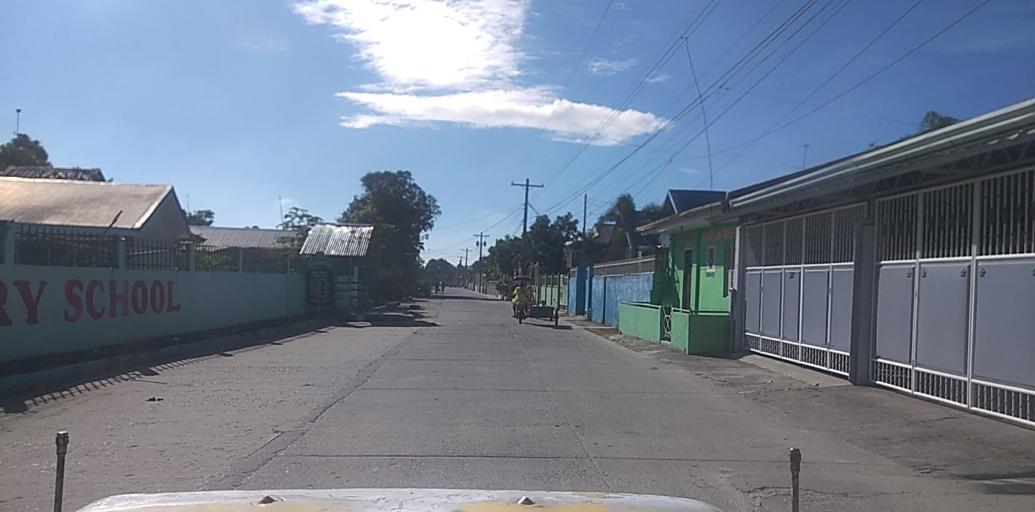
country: PH
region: Central Luzon
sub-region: Province of Pampanga
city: San Patricio
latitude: 15.1093
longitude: 120.7122
